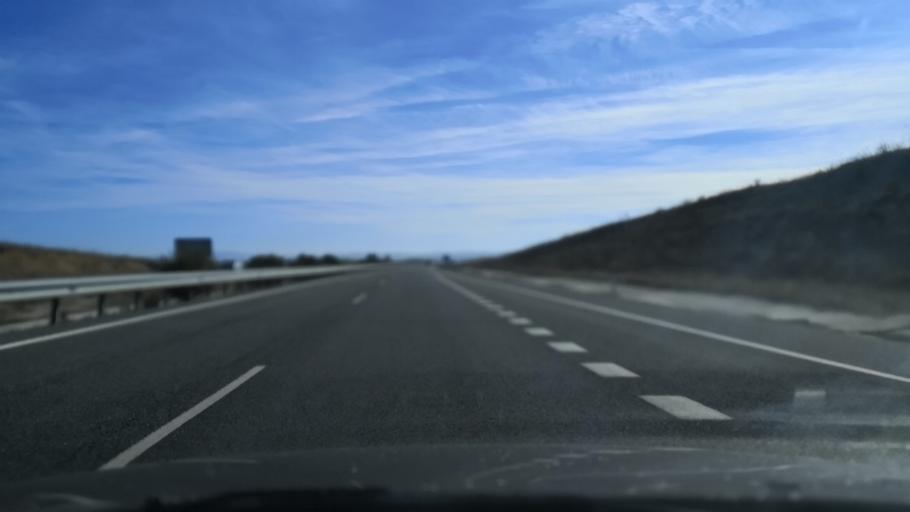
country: ES
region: Castille and Leon
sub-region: Provincia de Avila
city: Crespos
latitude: 40.8421
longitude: -4.9583
